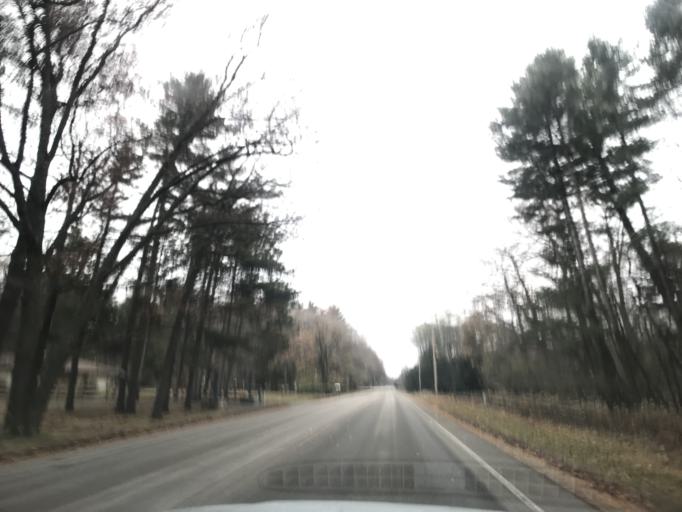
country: US
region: Wisconsin
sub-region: Marinette County
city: Marinette
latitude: 45.0688
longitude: -87.6193
